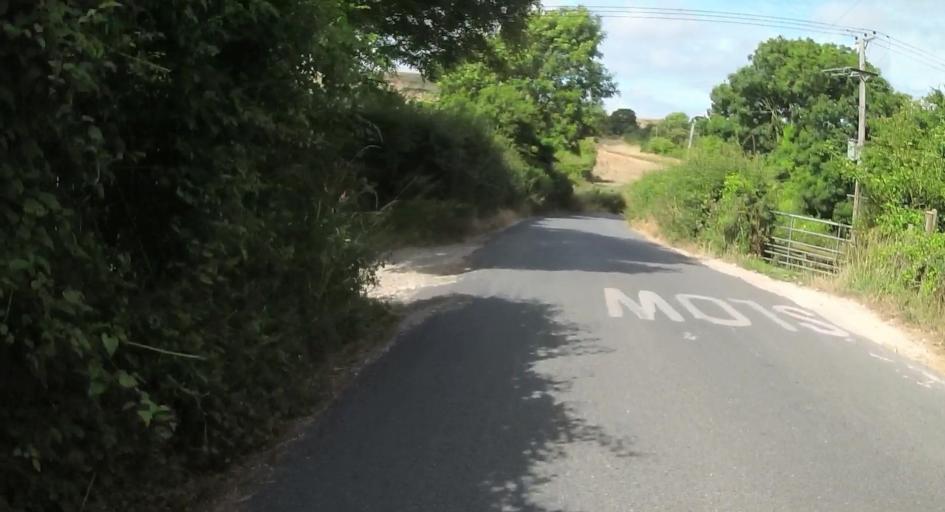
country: GB
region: England
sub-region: Dorset
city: Swanage
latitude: 50.6136
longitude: -1.9812
